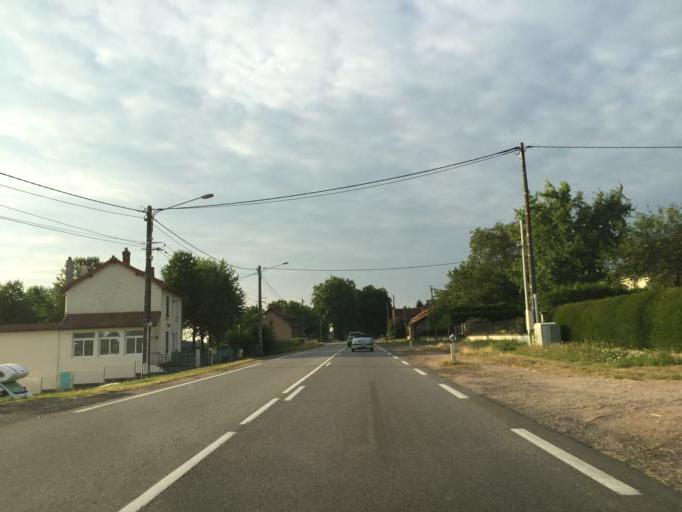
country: FR
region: Auvergne
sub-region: Departement de l'Allier
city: Varennes-sur-Allier
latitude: 46.3343
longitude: 3.3841
